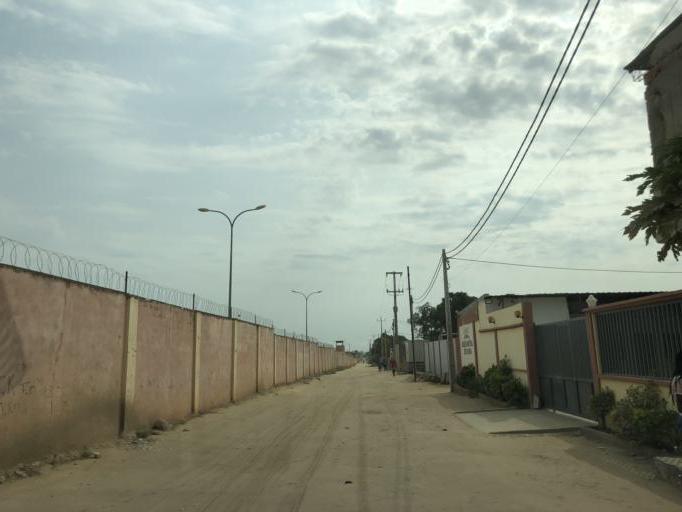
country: AO
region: Luanda
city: Luanda
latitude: -8.8962
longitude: 13.3545
